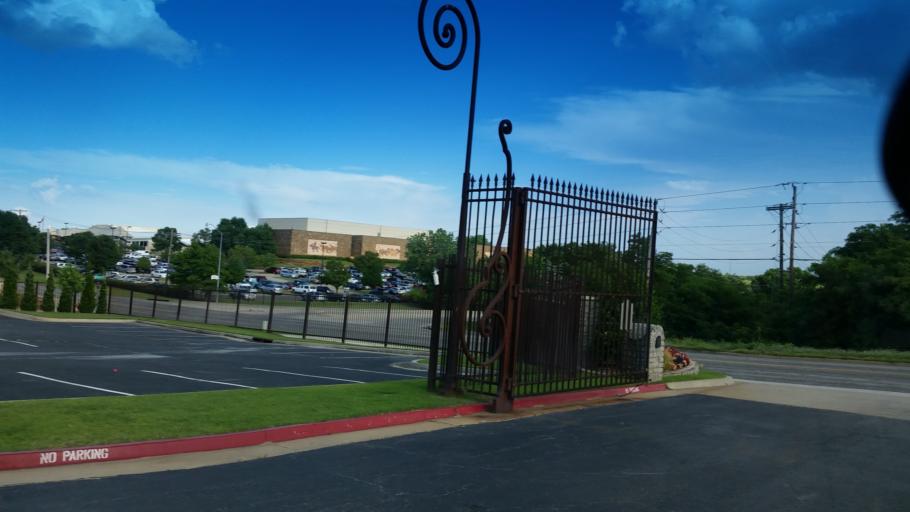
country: US
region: Oklahoma
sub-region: Oklahoma County
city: Nichols Hills
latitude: 35.5372
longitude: -97.4861
